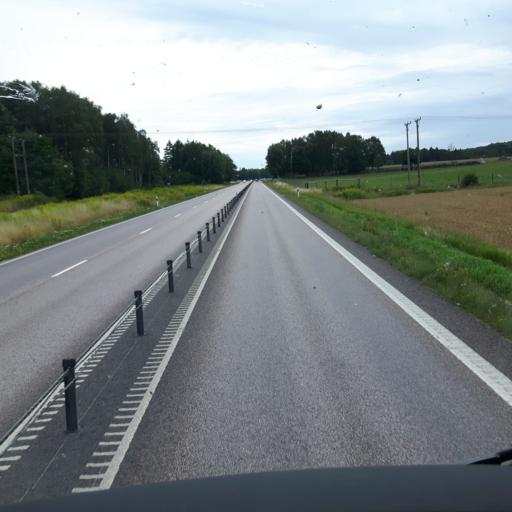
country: SE
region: Skane
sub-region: Hassleholms Kommun
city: Vinslov
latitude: 56.1059
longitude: 13.8729
